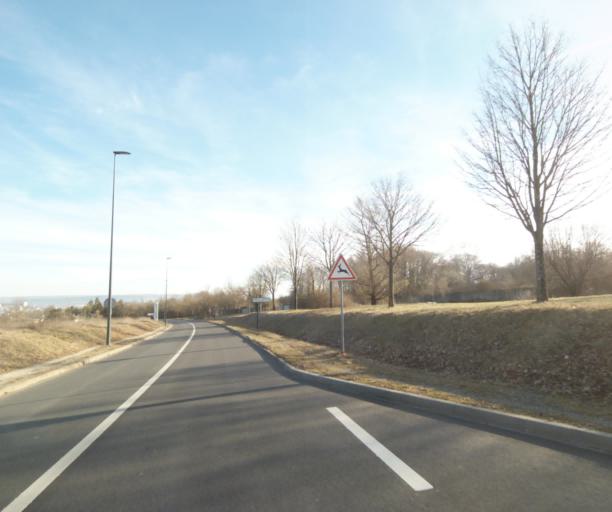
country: FR
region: Lorraine
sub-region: Departement de Meurthe-et-Moselle
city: Villers-les-Nancy
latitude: 48.6585
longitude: 6.1391
